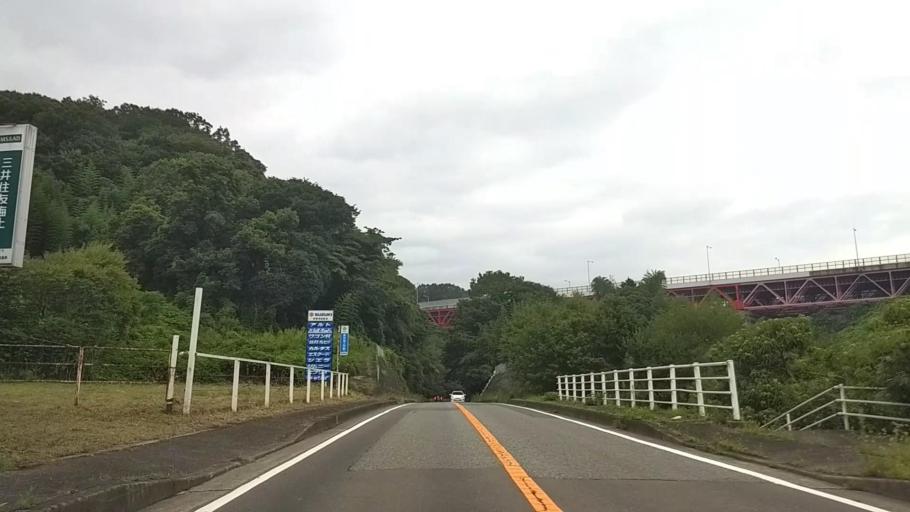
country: JP
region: Kanagawa
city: Hadano
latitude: 35.3385
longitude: 139.1963
